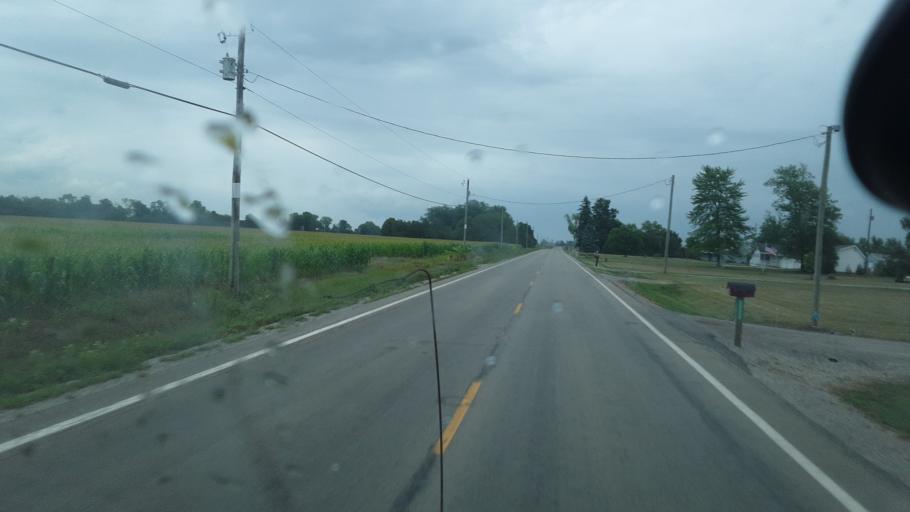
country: US
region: Ohio
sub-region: Defiance County
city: Hicksville
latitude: 41.2960
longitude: -84.7218
